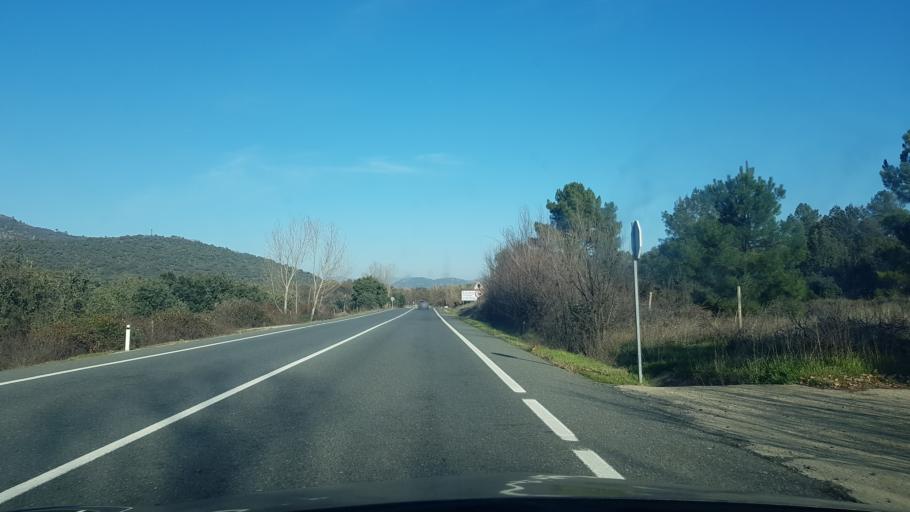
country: ES
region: Madrid
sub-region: Provincia de Madrid
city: Rozas de Puerto Real
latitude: 40.3321
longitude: -4.4698
